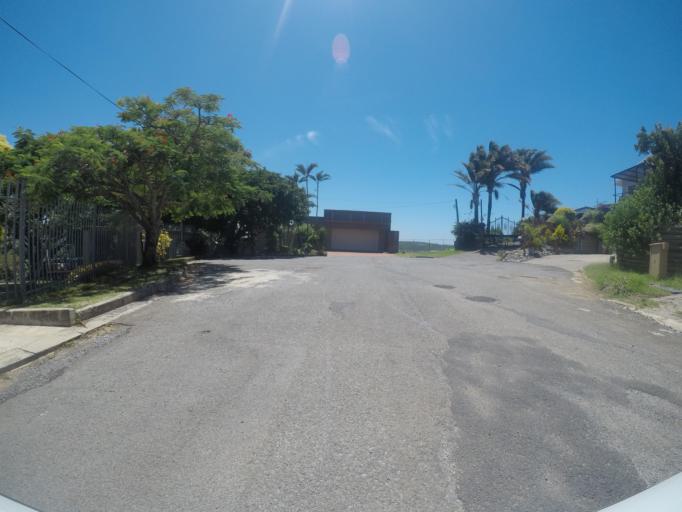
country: ZA
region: Eastern Cape
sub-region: Buffalo City Metropolitan Municipality
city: East London
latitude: -32.9325
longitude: 27.9951
